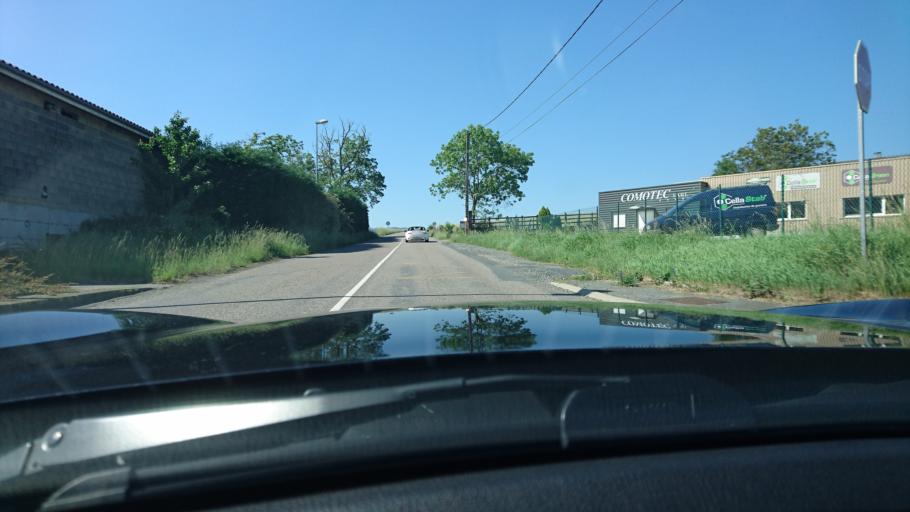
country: FR
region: Rhone-Alpes
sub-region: Departement du Rhone
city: Bessenay
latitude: 45.7768
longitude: 4.5625
